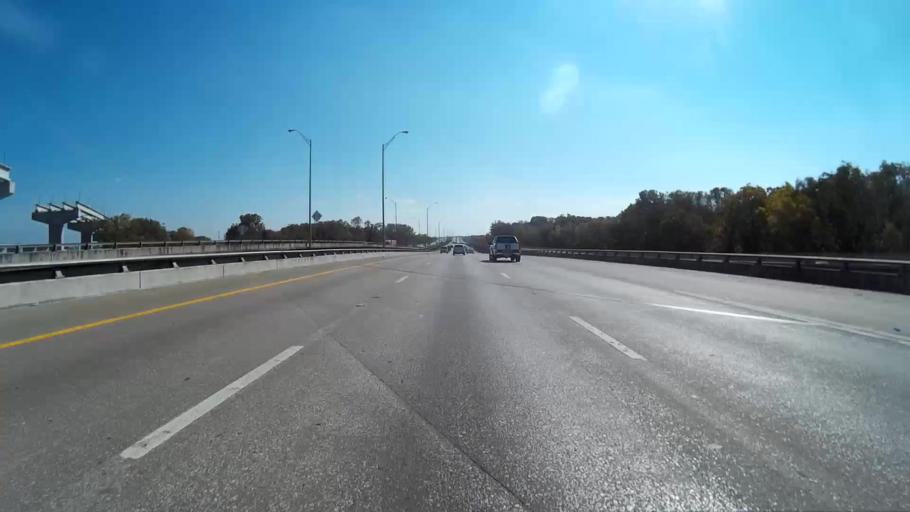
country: US
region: Texas
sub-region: Dallas County
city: Dallas
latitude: 32.7468
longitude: -96.7691
